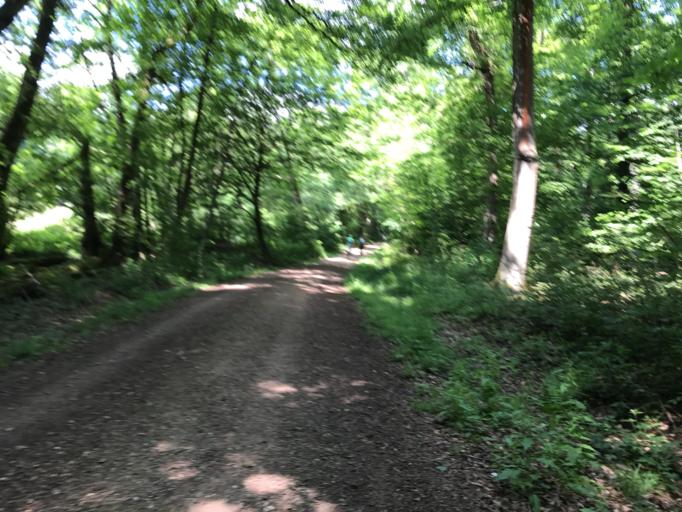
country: DE
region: Hesse
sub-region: Regierungsbezirk Darmstadt
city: Walluf
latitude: 50.0706
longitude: 8.1358
